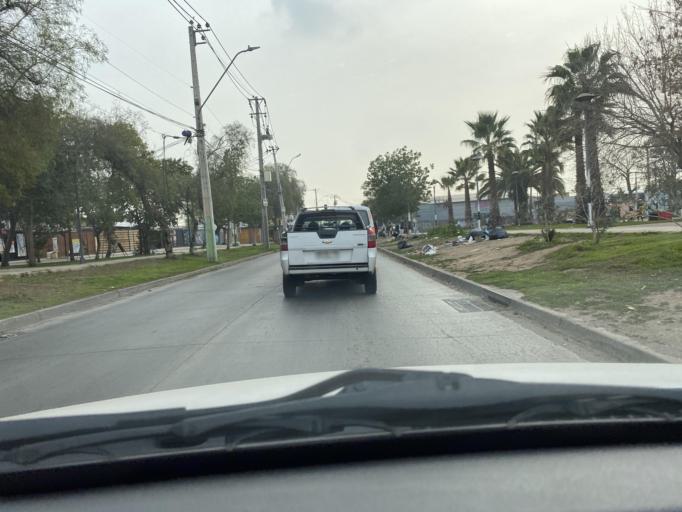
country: CL
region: Santiago Metropolitan
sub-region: Provincia de Santiago
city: Santiago
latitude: -33.5185
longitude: -70.6276
